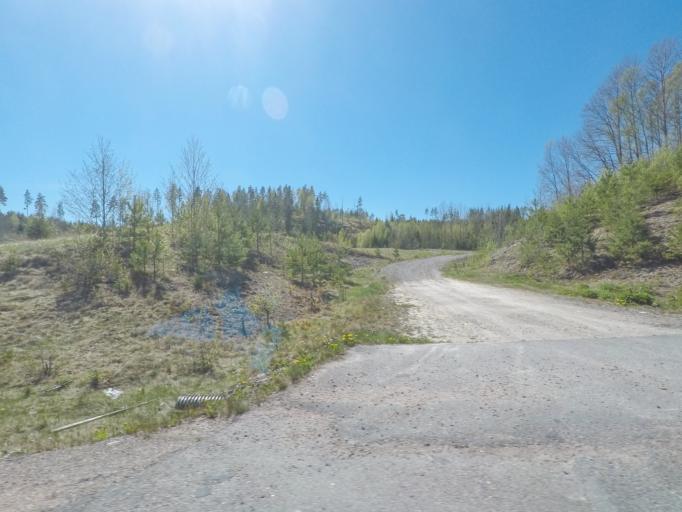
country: FI
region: Uusimaa
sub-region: Helsinki
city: Sammatti
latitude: 60.3764
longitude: 23.8072
